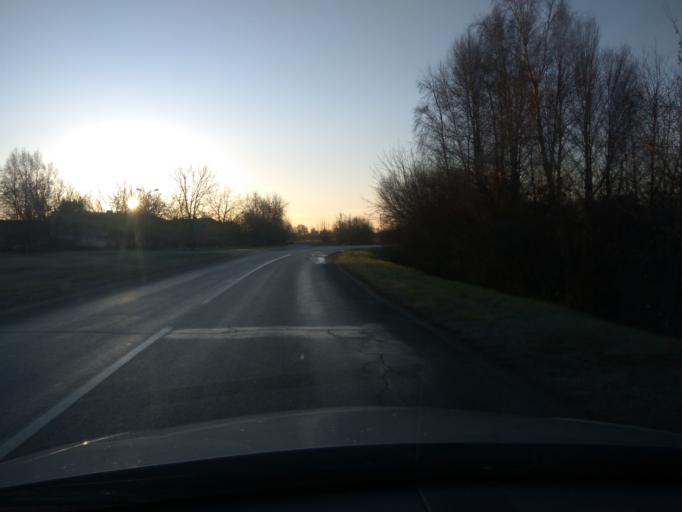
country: LV
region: Kuldigas Rajons
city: Kuldiga
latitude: 56.9669
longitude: 22.0025
